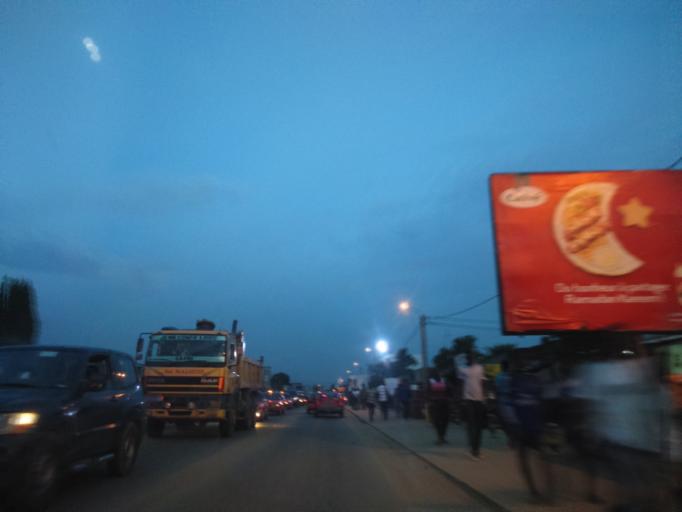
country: CI
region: Lagunes
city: Abobo
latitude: 5.4097
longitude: -3.9936
